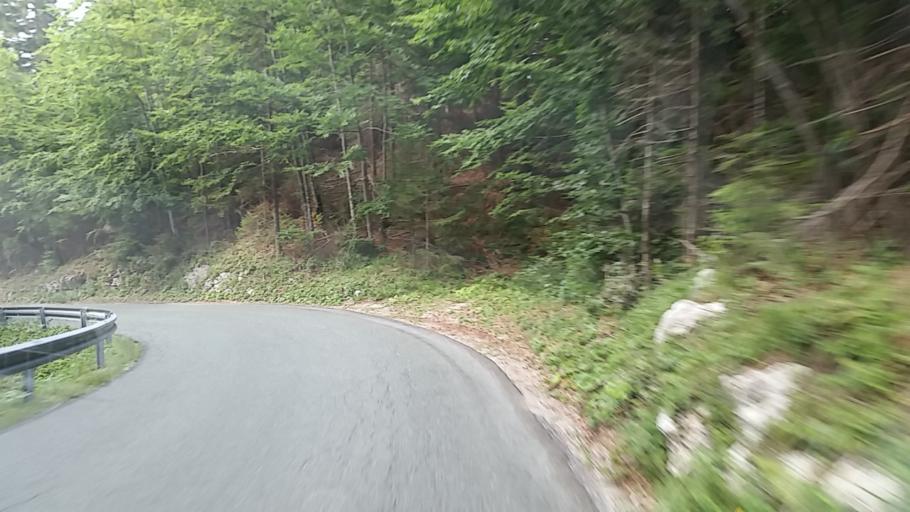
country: SI
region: Bohinj
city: Bohinjska Bistrica
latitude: 46.2630
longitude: 14.0076
